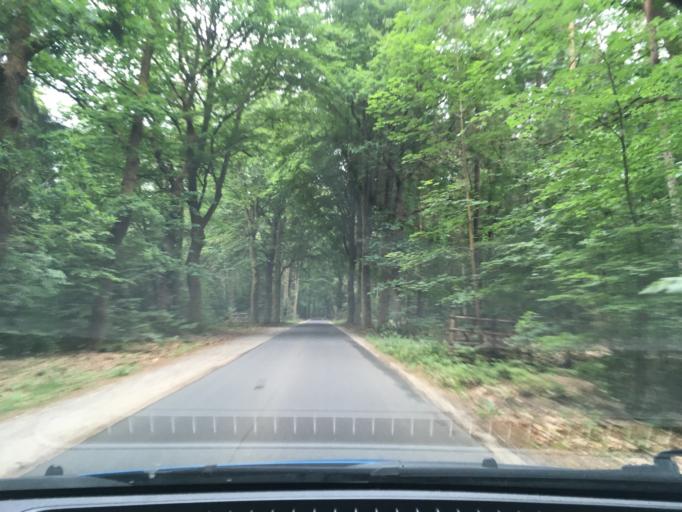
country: DE
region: Lower Saxony
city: Gohrde
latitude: 53.1127
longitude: 10.8798
